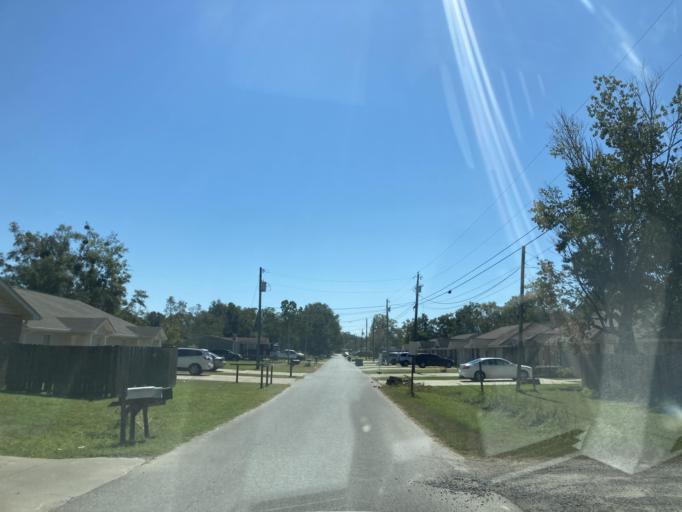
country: US
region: Mississippi
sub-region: Jackson County
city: Saint Martin
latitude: 30.4611
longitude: -88.8780
